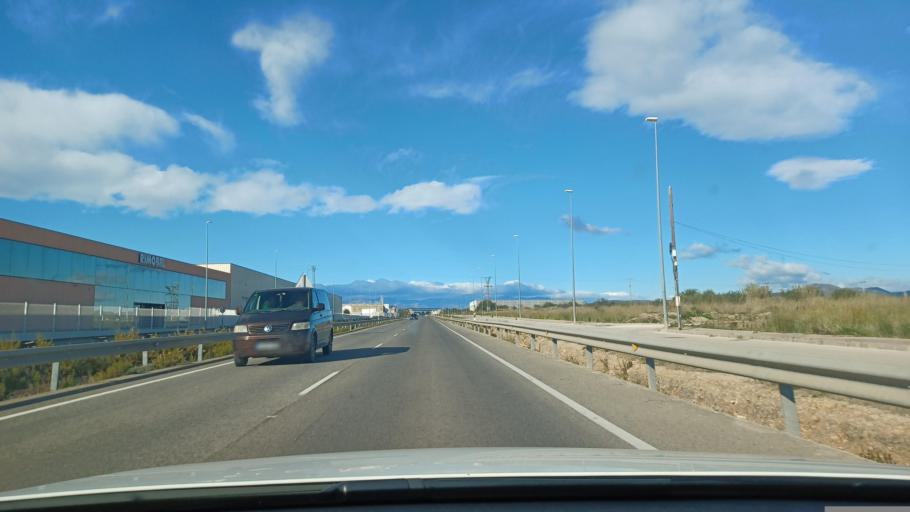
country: ES
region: Valencia
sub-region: Provincia de Castello
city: Vinaros
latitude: 40.4895
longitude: 0.4685
